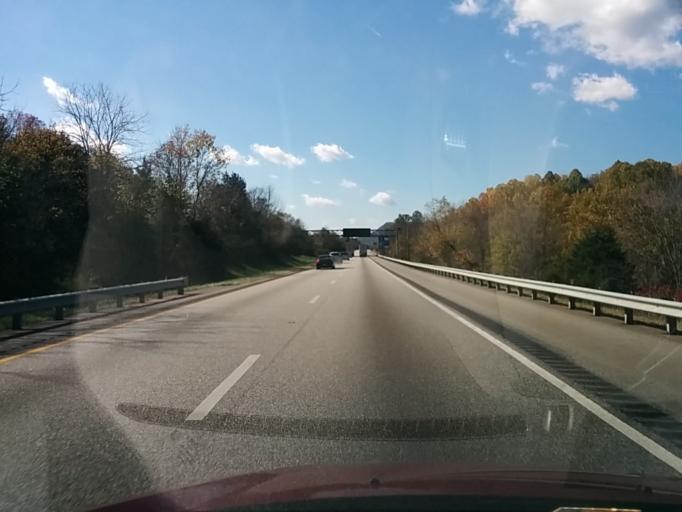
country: US
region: Virginia
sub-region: Botetourt County
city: Daleville
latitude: 37.4157
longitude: -79.8865
